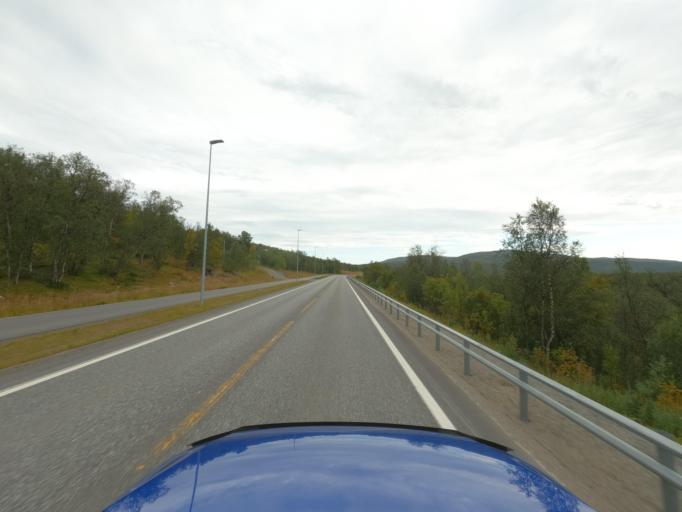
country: NO
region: Finnmark Fylke
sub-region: Kvalsund
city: Kvalsund
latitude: 70.4376
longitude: 24.4822
